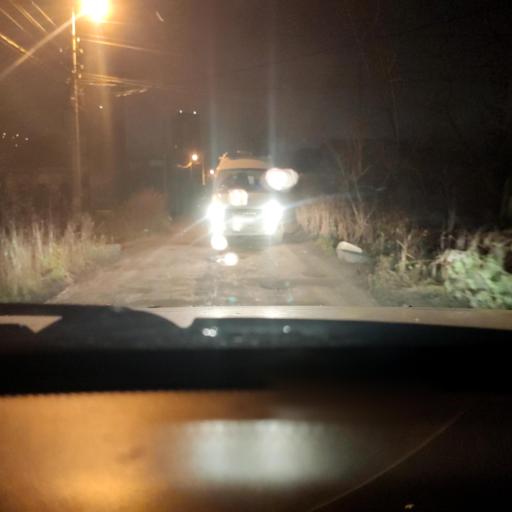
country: RU
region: Perm
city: Kondratovo
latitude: 57.9642
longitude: 56.1485
